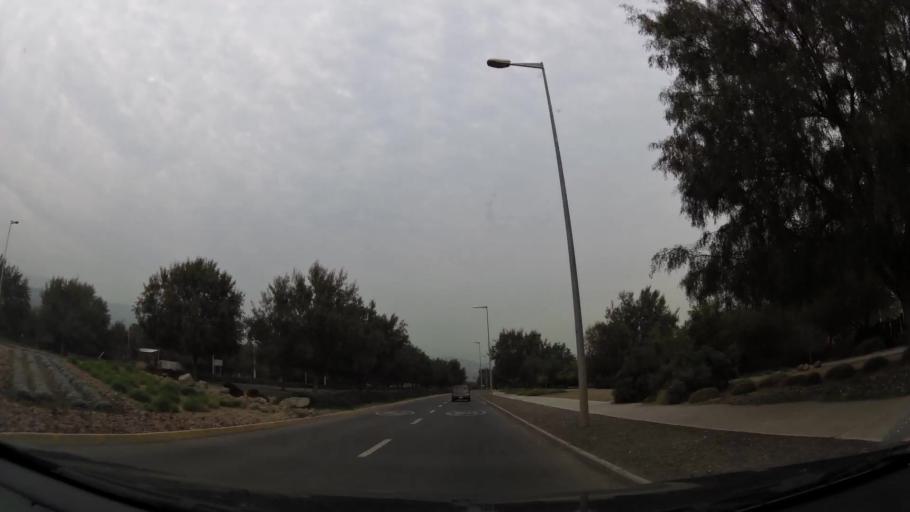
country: CL
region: Santiago Metropolitan
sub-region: Provincia de Chacabuco
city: Chicureo Abajo
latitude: -33.2607
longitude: -70.6266
